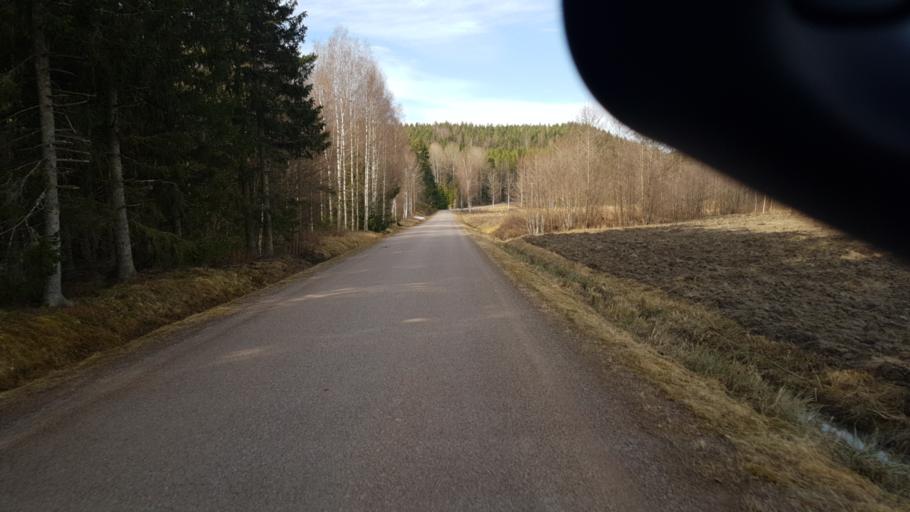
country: SE
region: Vaermland
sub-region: Arvika Kommun
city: Arvika
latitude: 59.5485
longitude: 12.5482
